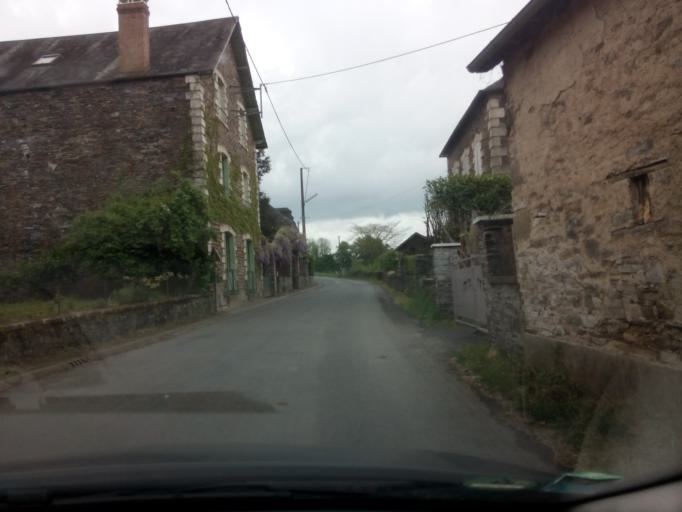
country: FR
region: Limousin
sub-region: Departement de la Correze
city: Allassac
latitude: 45.2756
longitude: 1.4590
